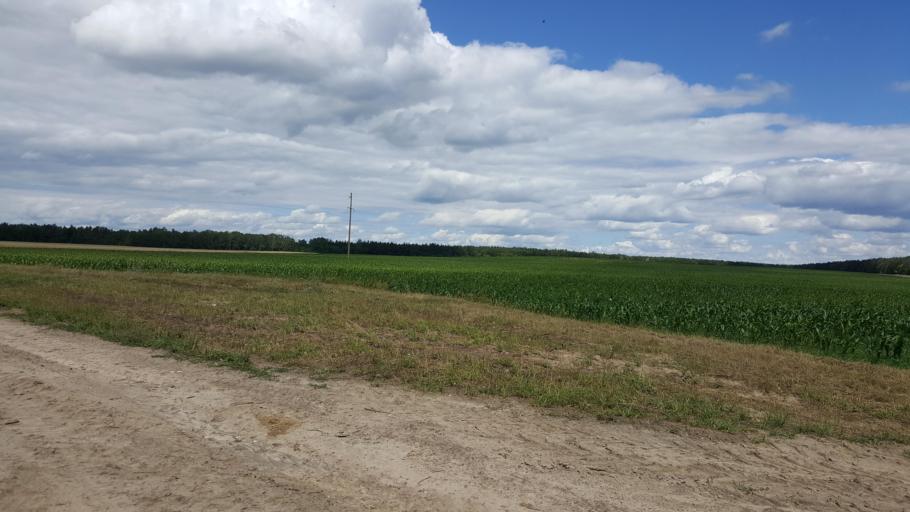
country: BY
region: Brest
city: Kamyanyets
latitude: 52.3359
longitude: 23.9116
